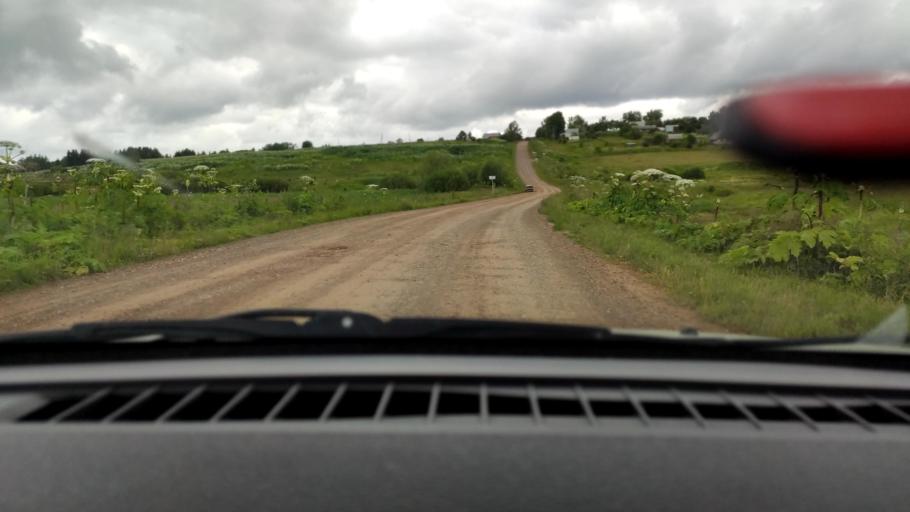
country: RU
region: Perm
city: Chaykovskaya
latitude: 58.1388
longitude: 55.5631
